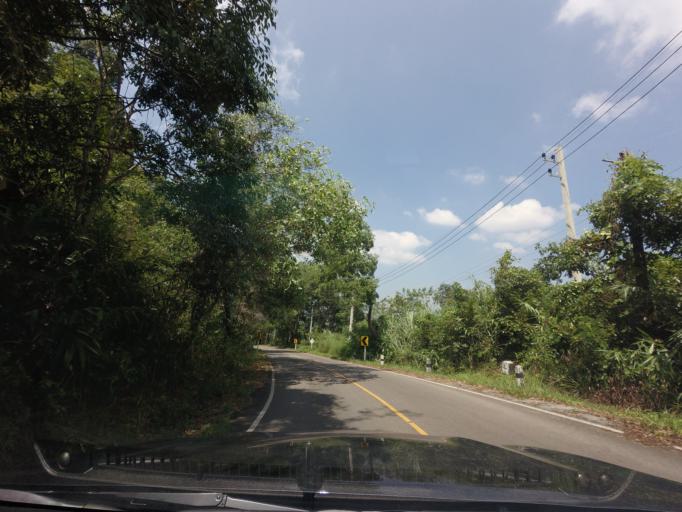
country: TH
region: Loei
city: Na Haeo
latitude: 17.4937
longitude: 100.8959
